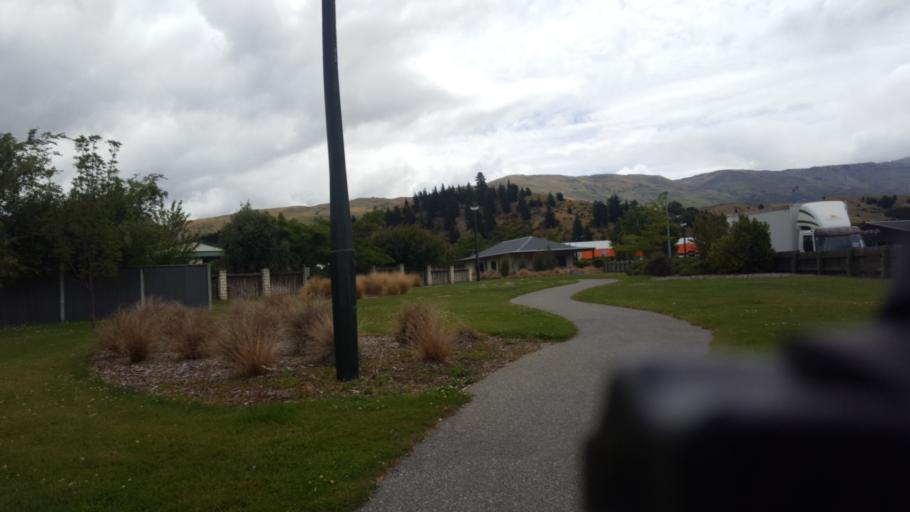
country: NZ
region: Otago
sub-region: Queenstown-Lakes District
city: Wanaka
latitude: -45.0378
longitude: 169.1936
